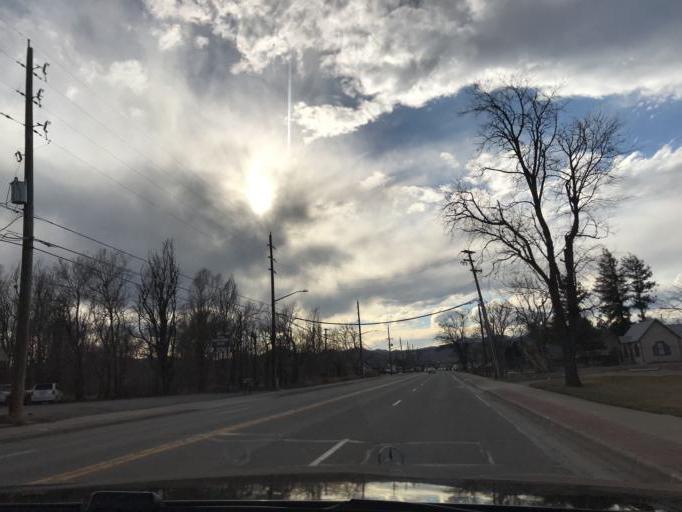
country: US
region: Colorado
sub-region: Jefferson County
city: Applewood
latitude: 39.7782
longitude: -105.1269
